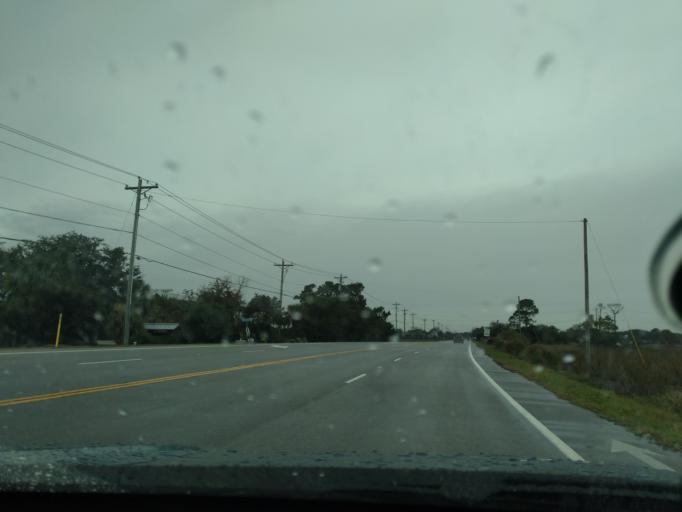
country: US
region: South Carolina
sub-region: Charleston County
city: Folly Beach
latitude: 32.6787
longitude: -79.9540
